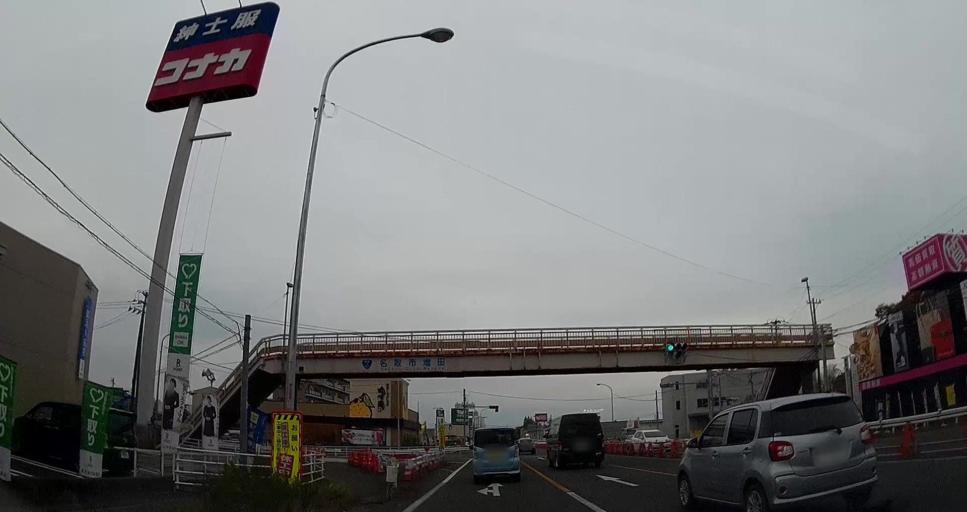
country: JP
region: Miyagi
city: Iwanuma
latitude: 38.1718
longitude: 140.8901
